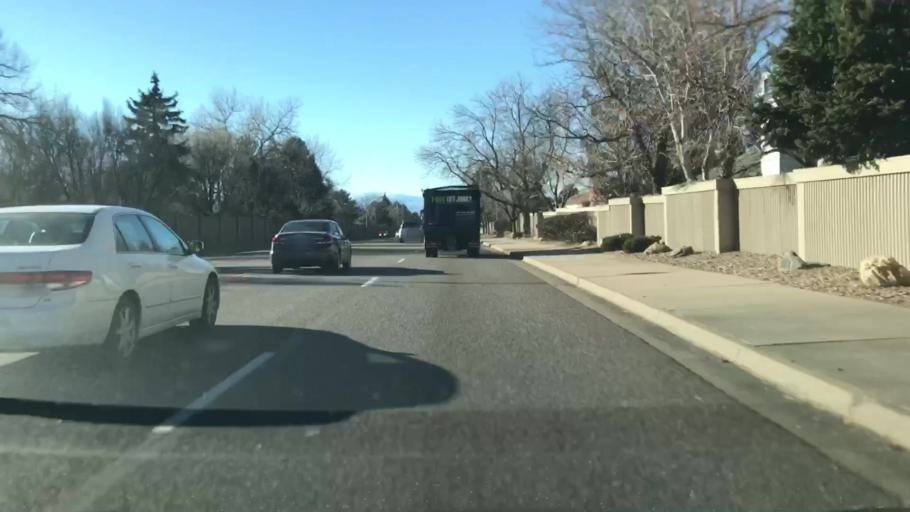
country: US
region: Colorado
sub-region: Adams County
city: Aurora
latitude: 39.6749
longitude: -104.8582
